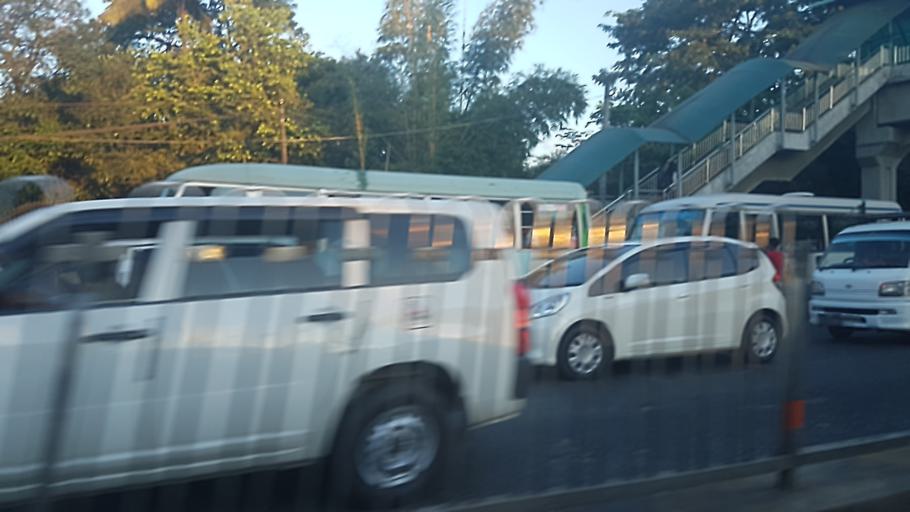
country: MM
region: Yangon
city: Yangon
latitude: 16.9278
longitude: 96.1314
